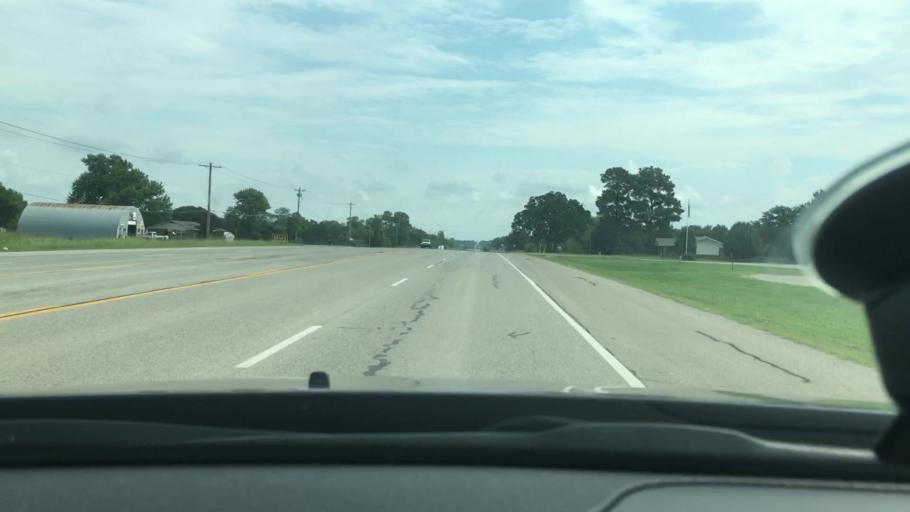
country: US
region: Oklahoma
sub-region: Carter County
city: Dickson
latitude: 34.1871
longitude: -96.9983
